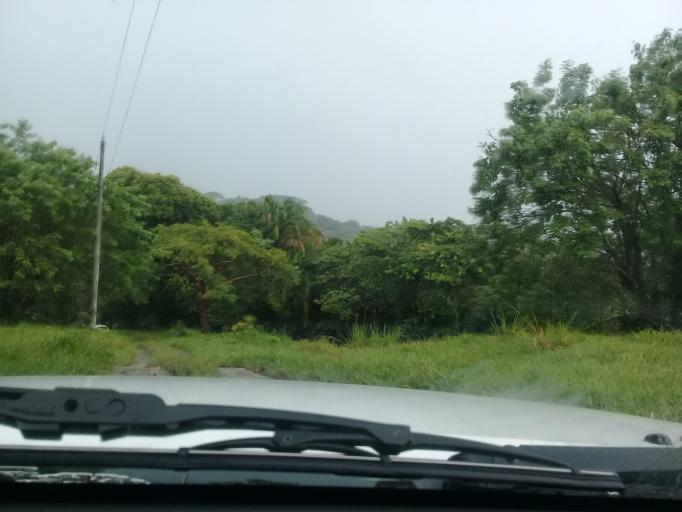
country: MX
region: Veracruz
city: Santiago Tuxtla
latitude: 18.4610
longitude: -95.3246
